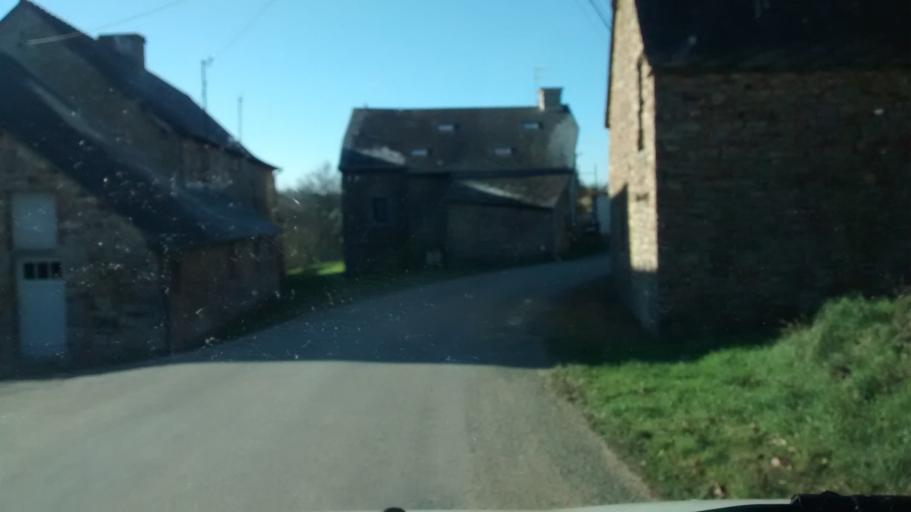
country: FR
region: Brittany
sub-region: Departement d'Ille-et-Vilaine
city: La Bouexiere
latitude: 48.2010
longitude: -1.4608
